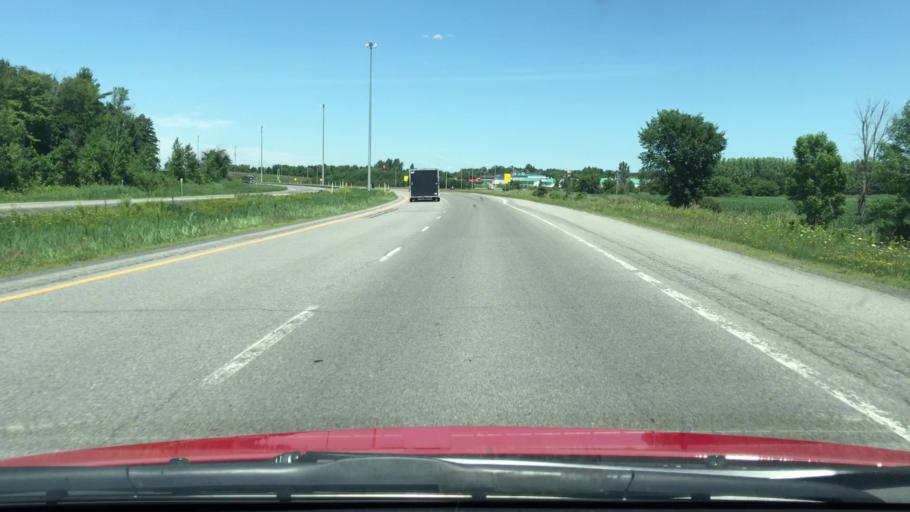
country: CA
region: Quebec
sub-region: Monteregie
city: Napierville
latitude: 45.1875
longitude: -73.4537
